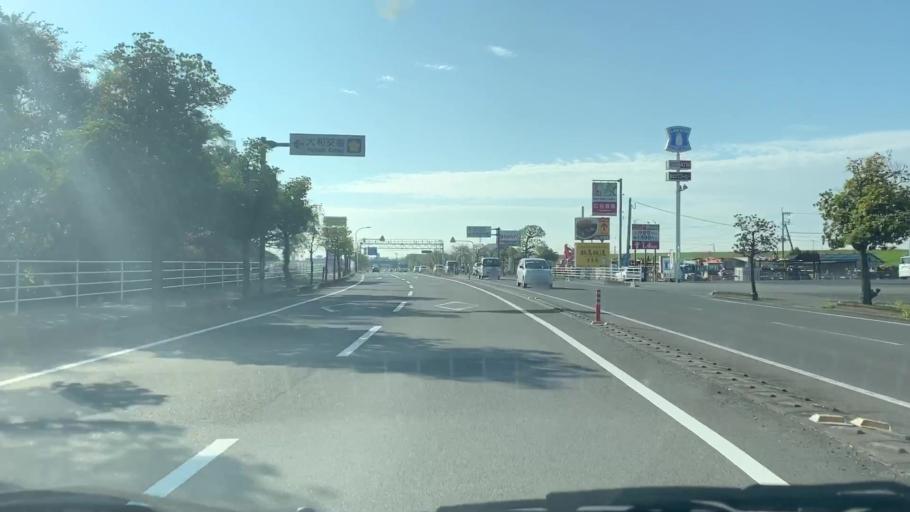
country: JP
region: Saga Prefecture
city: Saga-shi
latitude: 33.3132
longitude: 130.2757
